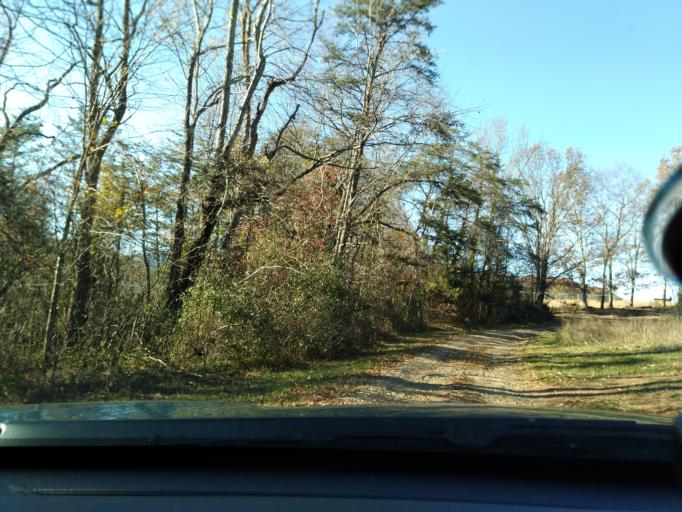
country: US
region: Virginia
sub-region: Floyd County
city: Floyd
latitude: 36.8349
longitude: -80.1841
